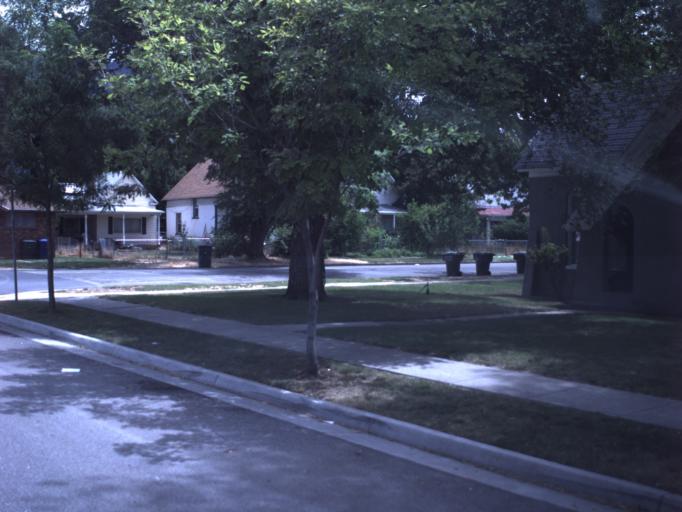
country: US
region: Utah
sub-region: Weber County
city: Ogden
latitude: 41.2102
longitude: -111.9683
